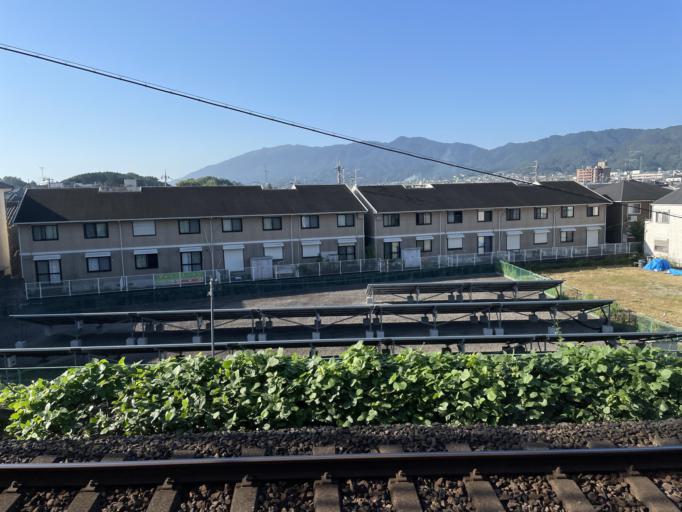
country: JP
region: Nara
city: Tawaramoto
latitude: 34.5404
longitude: 135.7079
